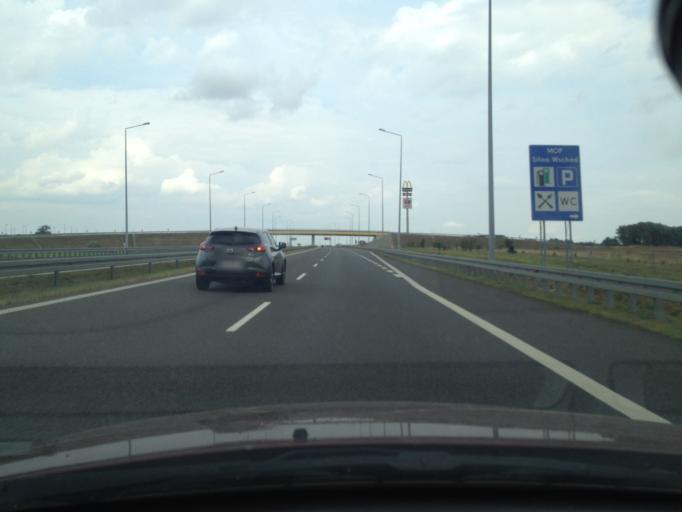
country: PL
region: West Pomeranian Voivodeship
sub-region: Powiat pyrzycki
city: Kozielice
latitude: 53.0471
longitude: 14.8661
